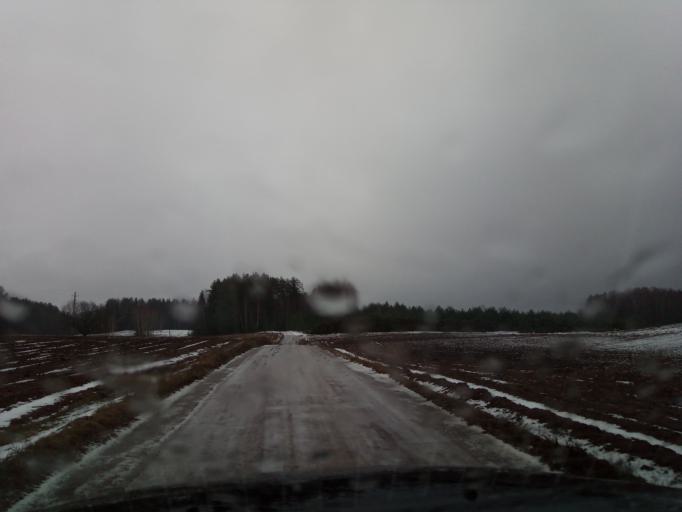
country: LT
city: Svencioneliai
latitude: 55.3425
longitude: 25.8433
